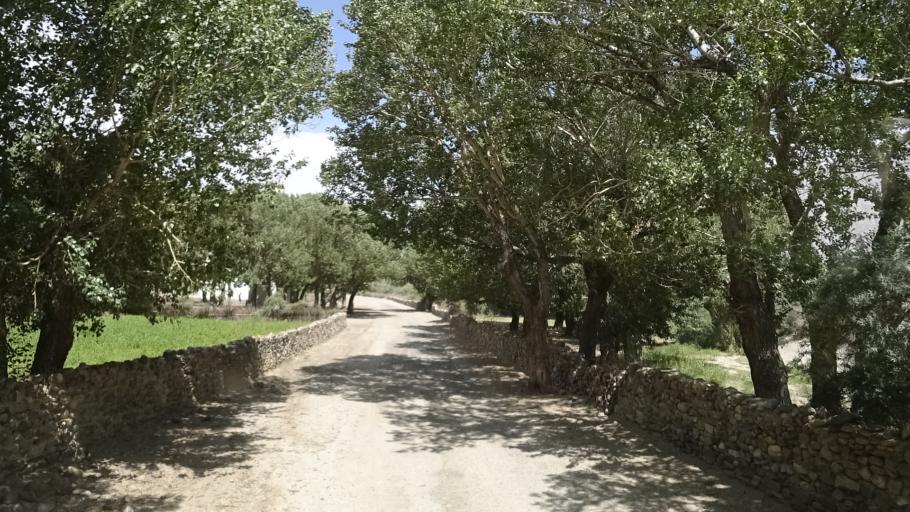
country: AF
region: Badakhshan
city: Khandud
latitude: 36.9127
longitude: 72.1814
